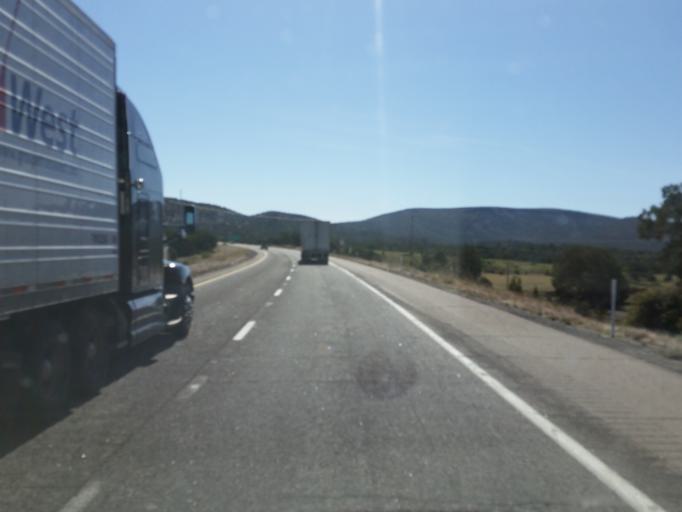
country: US
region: Arizona
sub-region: Mohave County
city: Peach Springs
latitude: 35.1808
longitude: -113.4607
